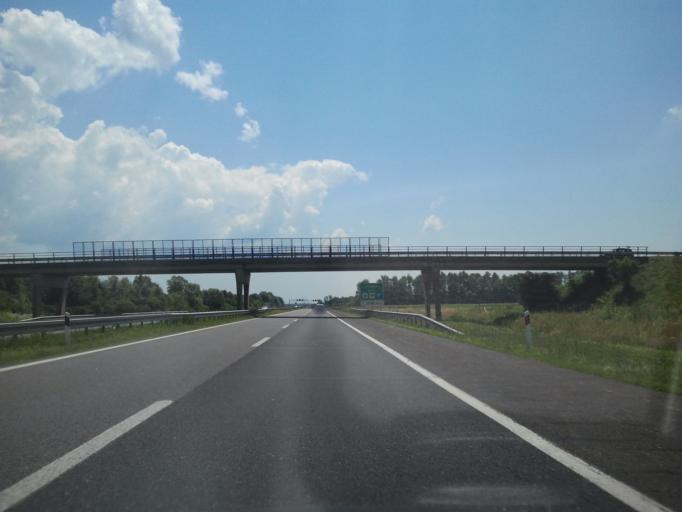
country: HR
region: Zagrebacka
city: Kriz
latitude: 45.6516
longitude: 16.4988
